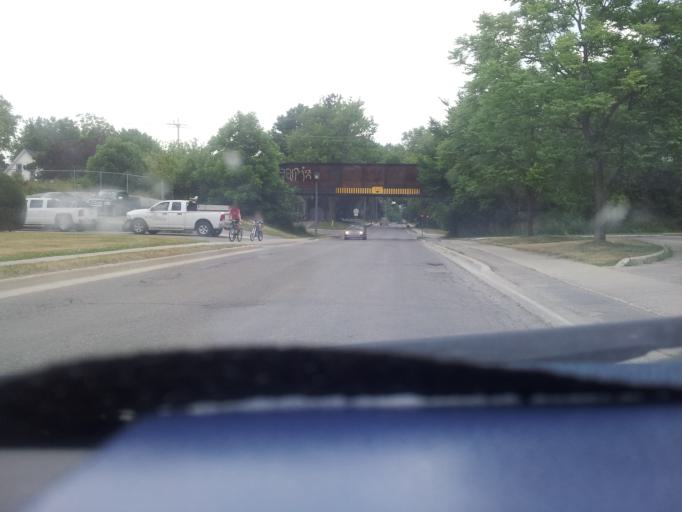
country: CA
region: Ontario
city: Stratford
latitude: 43.3676
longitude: -80.9847
